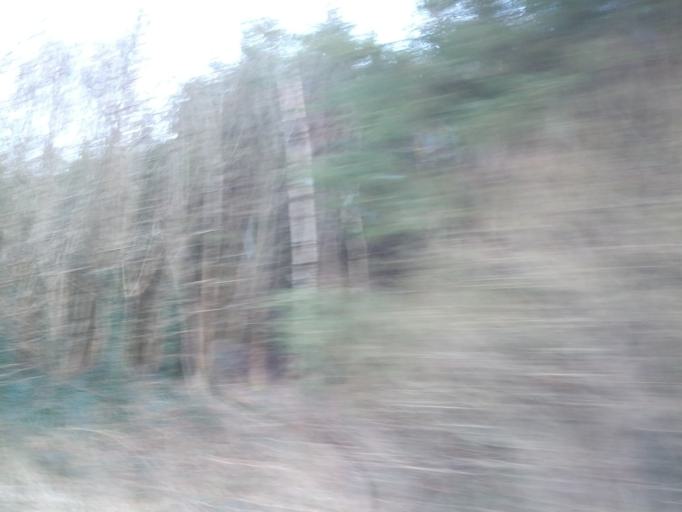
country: IE
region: Connaught
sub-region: County Galway
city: Athenry
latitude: 53.3556
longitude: -8.6691
